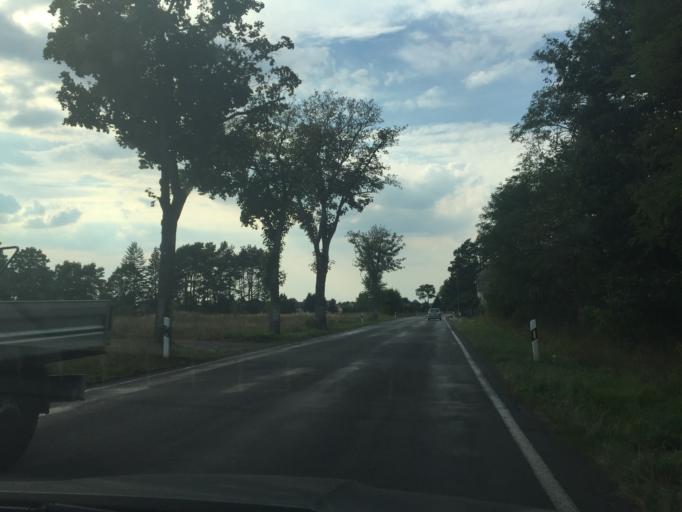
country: DE
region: Brandenburg
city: Spreenhagen
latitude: 52.3549
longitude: 13.8539
